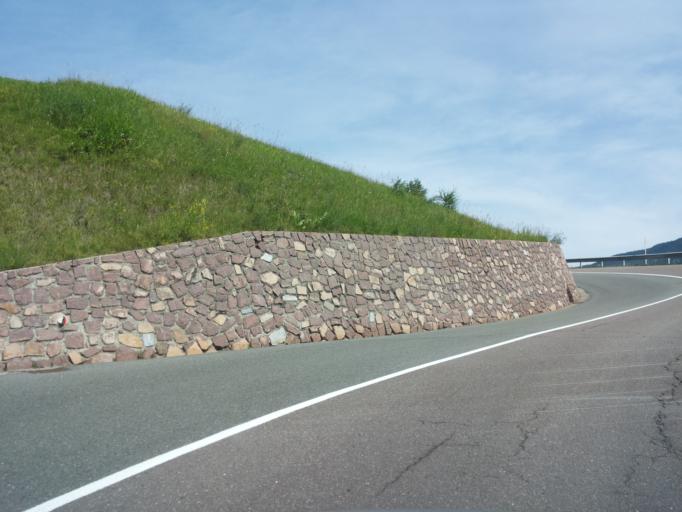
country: IT
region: Trentino-Alto Adige
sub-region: Bolzano
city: Ortisei
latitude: 46.5741
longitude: 11.6314
